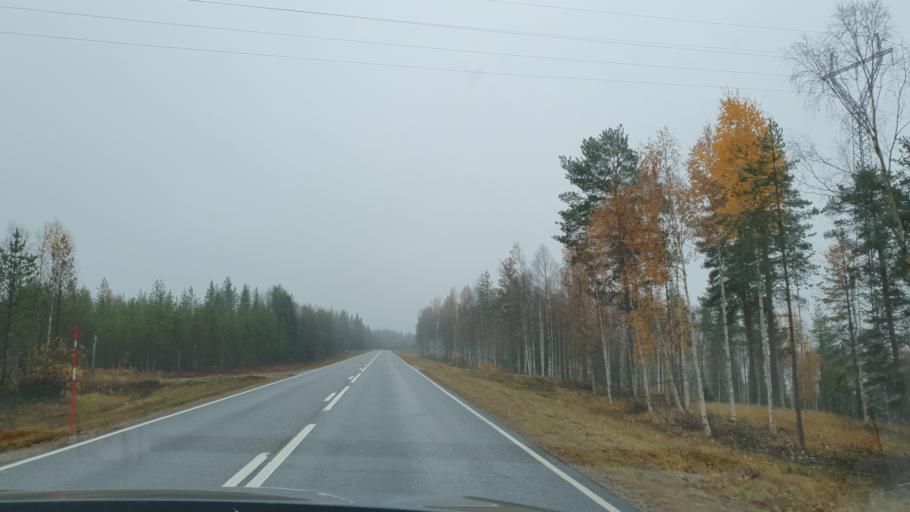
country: FI
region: Lapland
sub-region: Rovaniemi
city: Rovaniemi
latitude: 66.9568
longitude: 25.3510
